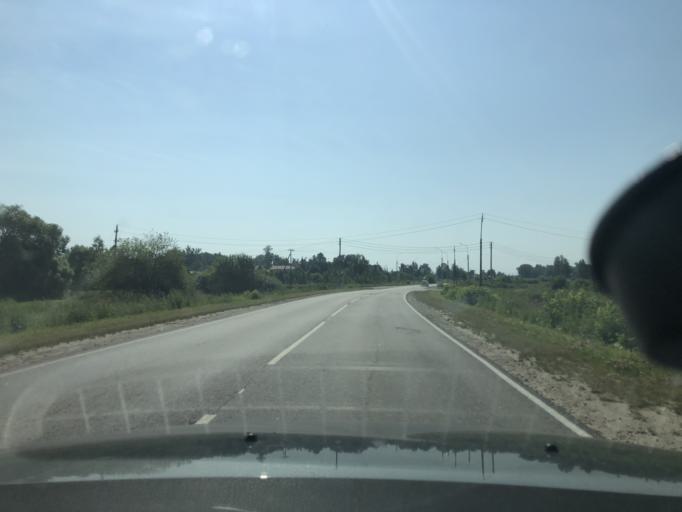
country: RU
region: Tula
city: Dubna
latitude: 54.1097
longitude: 37.1024
